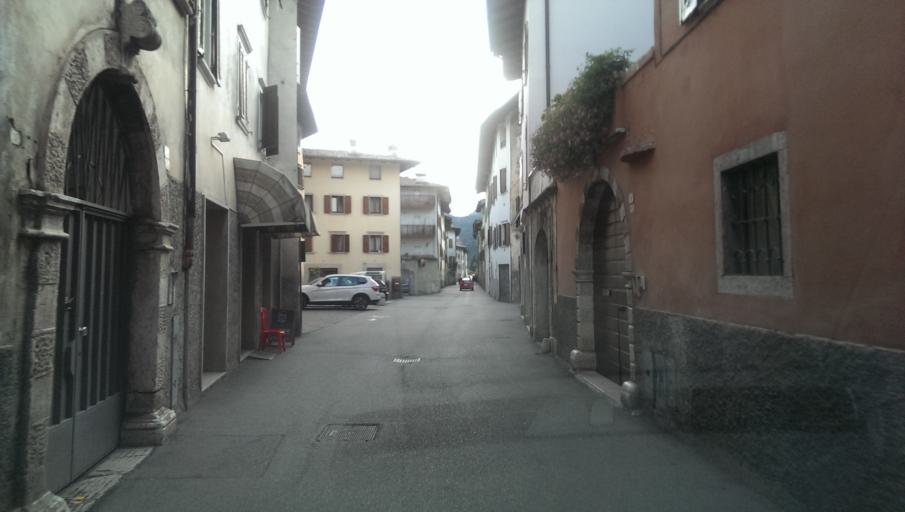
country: IT
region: Trentino-Alto Adige
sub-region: Provincia di Trento
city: Dro
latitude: 45.9608
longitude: 10.9095
